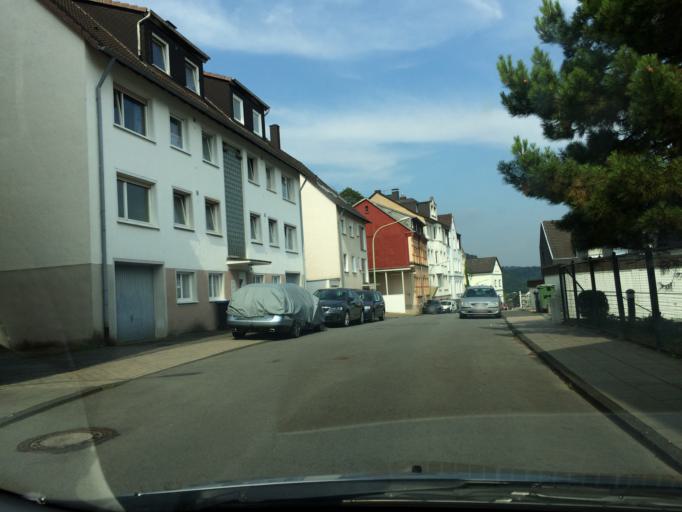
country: DE
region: North Rhine-Westphalia
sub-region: Regierungsbezirk Arnsberg
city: Nachrodt-Wiblingwerde
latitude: 51.3465
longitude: 7.5738
